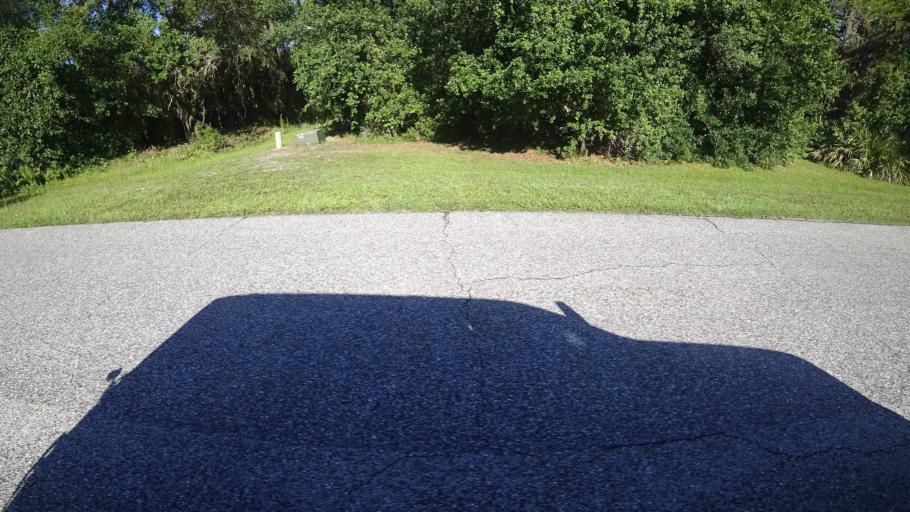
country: US
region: Florida
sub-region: Sarasota County
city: The Meadows
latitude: 27.4048
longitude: -82.3121
